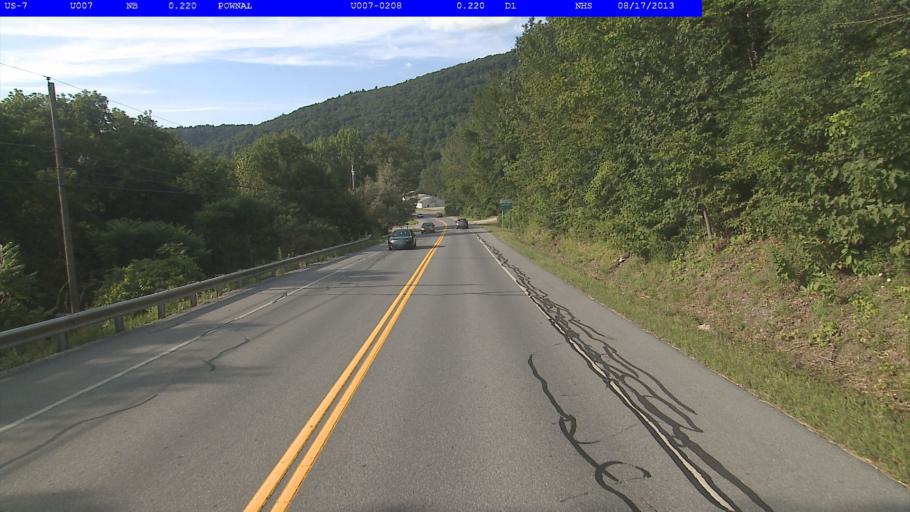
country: US
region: Massachusetts
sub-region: Berkshire County
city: Williamstown
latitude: 42.7481
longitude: -73.2142
